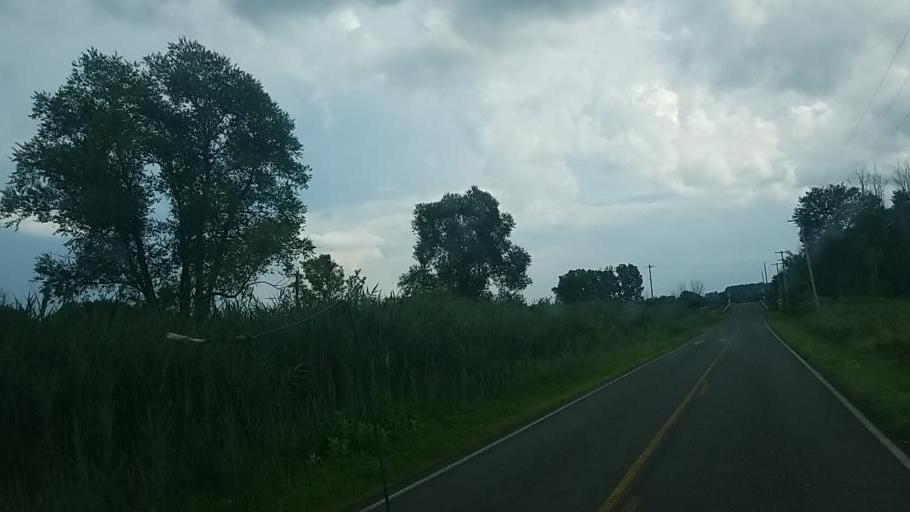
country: US
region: Ohio
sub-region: Medina County
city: Westfield Center
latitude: 41.0045
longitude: -81.9411
